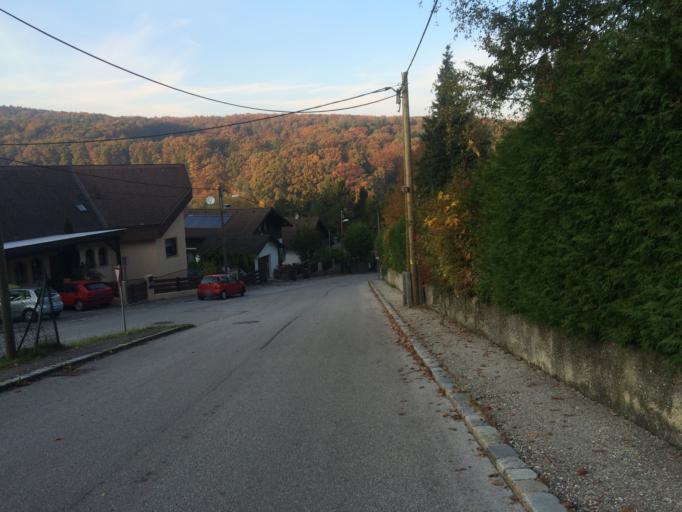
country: AT
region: Lower Austria
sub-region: Politischer Bezirk Wien-Umgebung
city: Gablitz
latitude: 48.2206
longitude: 16.1362
